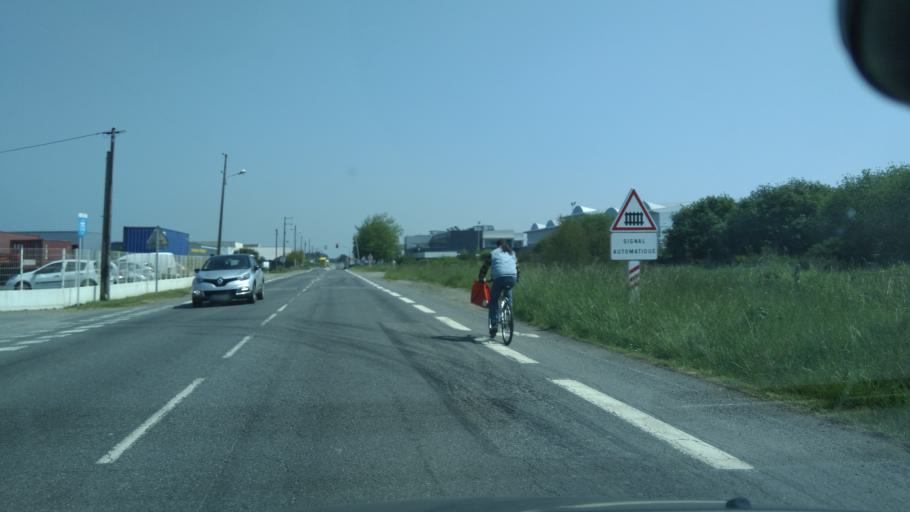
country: FR
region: Pays de la Loire
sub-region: Departement de la Loire-Atlantique
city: Trignac
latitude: 47.3137
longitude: -2.1712
